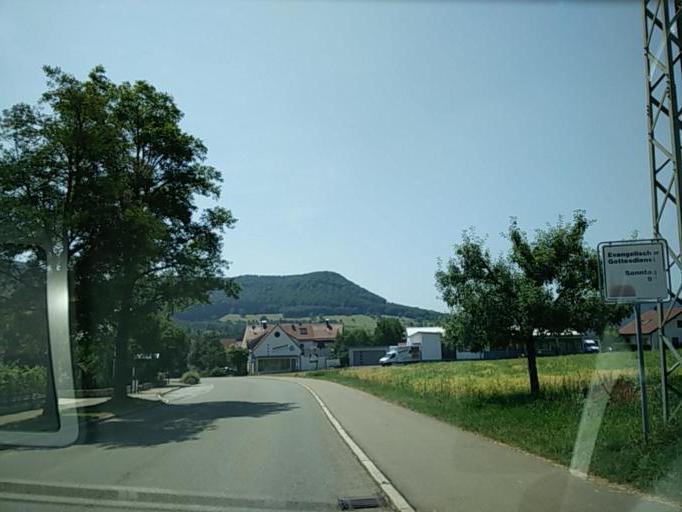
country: DE
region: Baden-Wuerttemberg
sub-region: Tuebingen Region
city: Gomaringen
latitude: 48.4187
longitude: 9.1106
